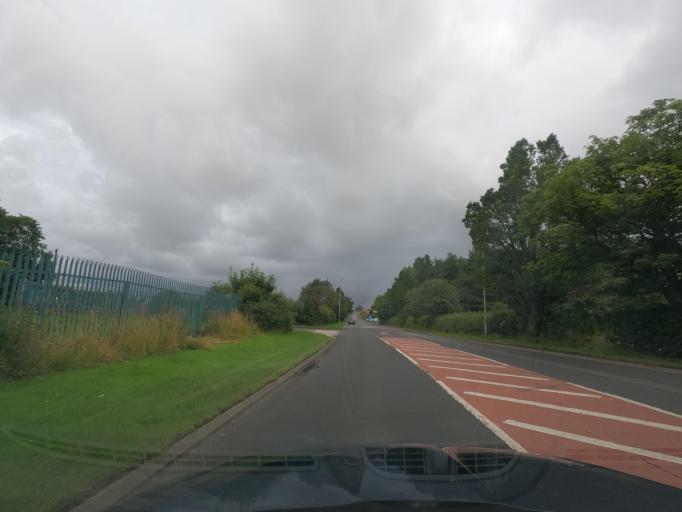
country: GB
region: England
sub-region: Northumberland
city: Berwick-Upon-Tweed
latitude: 55.7431
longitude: -1.9961
